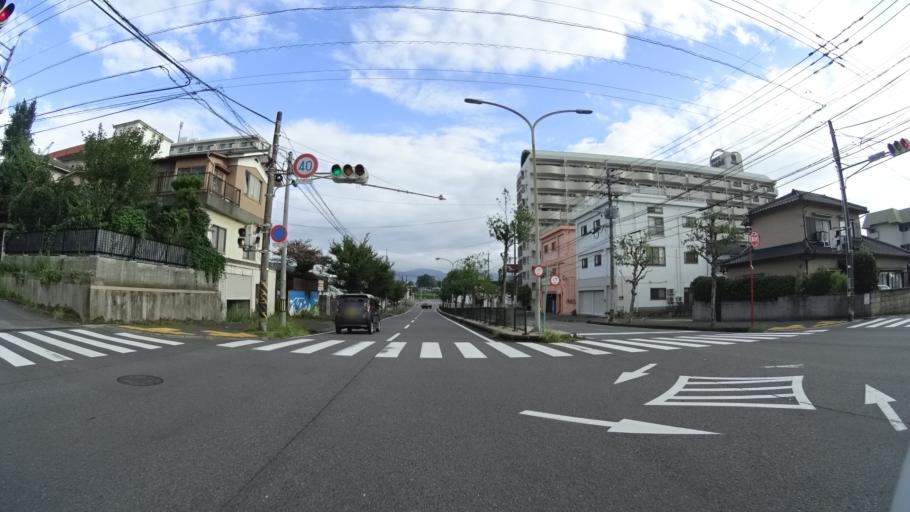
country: JP
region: Oita
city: Beppu
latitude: 33.3037
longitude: 131.4948
